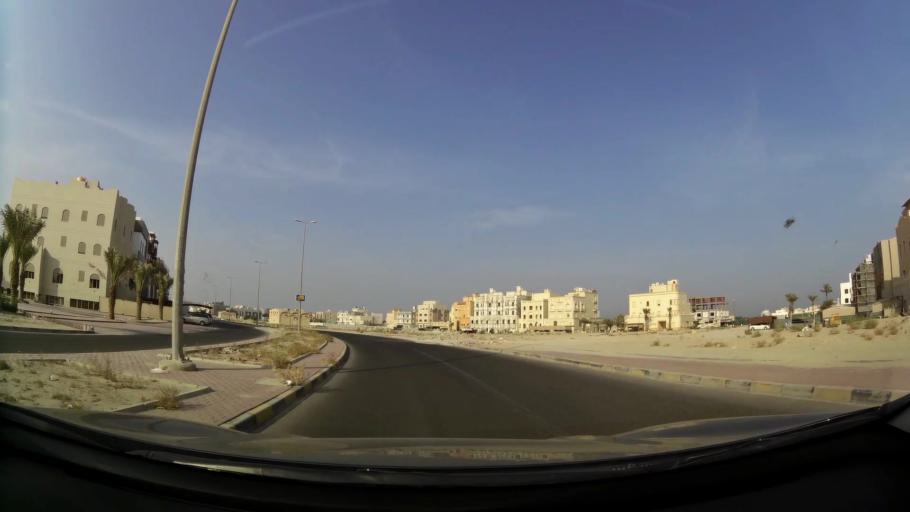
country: KW
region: Mubarak al Kabir
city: Mubarak al Kabir
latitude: 29.1873
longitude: 48.1066
